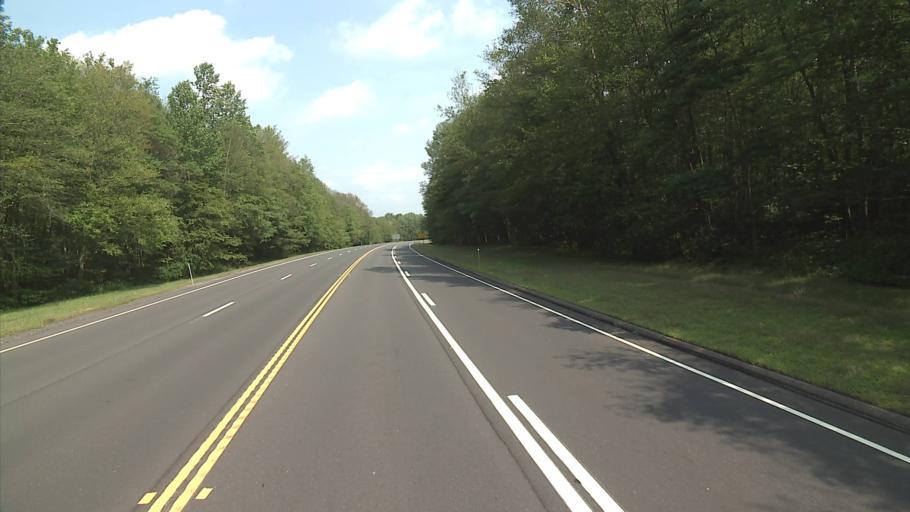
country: US
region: Connecticut
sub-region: Middlesex County
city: East Haddam
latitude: 41.4305
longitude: -72.4903
